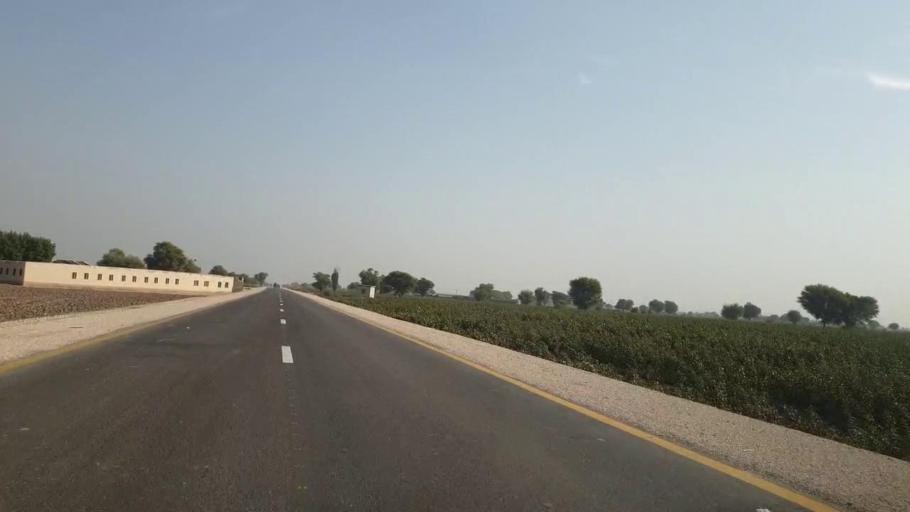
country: PK
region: Sindh
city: Sehwan
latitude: 26.4699
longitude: 67.7931
